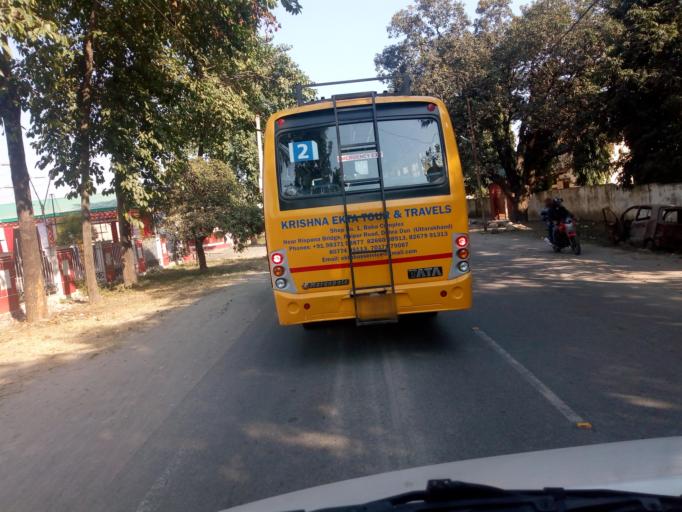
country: IN
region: Uttarakhand
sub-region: Dehradun
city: Harbatpur
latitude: 30.4414
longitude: 77.7275
